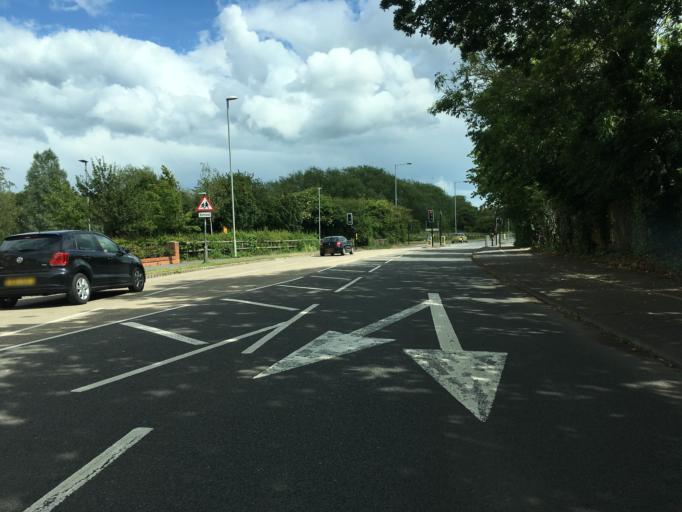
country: GB
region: England
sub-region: Borough of Swindon
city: Swindon
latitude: 51.5660
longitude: -1.7647
